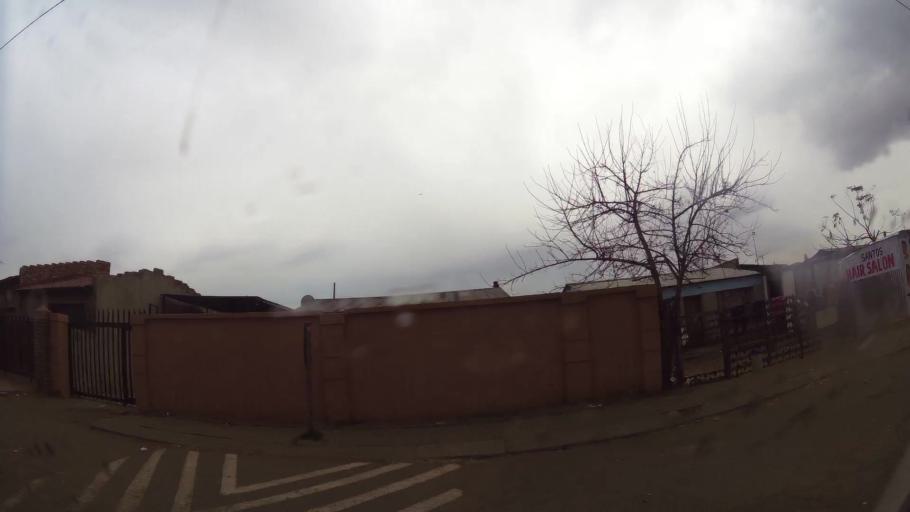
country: ZA
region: Gauteng
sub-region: Ekurhuleni Metropolitan Municipality
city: Germiston
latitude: -26.3381
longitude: 28.1440
